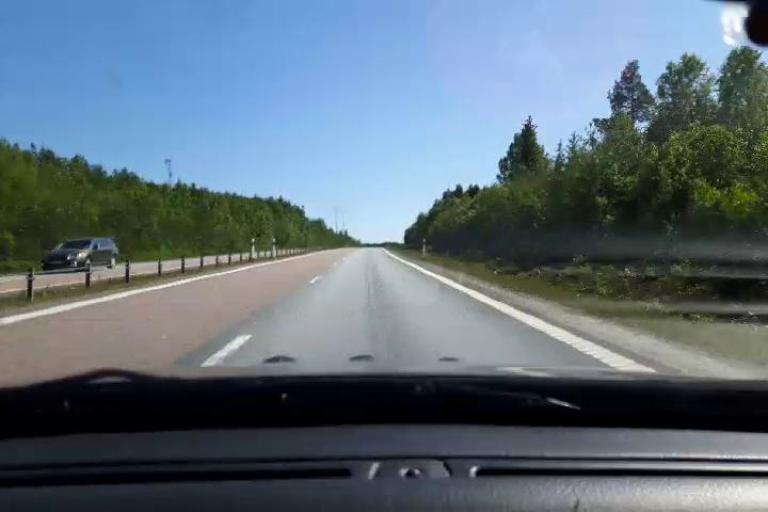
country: SE
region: Gaevleborg
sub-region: Hudiksvalls Kommun
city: Iggesund
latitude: 61.5090
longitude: 16.9856
